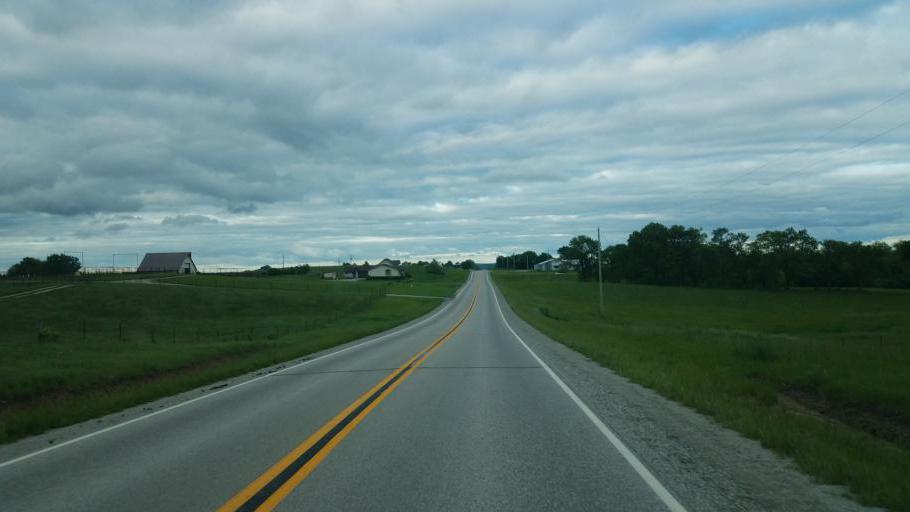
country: US
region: Iowa
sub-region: Decatur County
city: Lamoni
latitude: 40.6237
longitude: -93.8744
